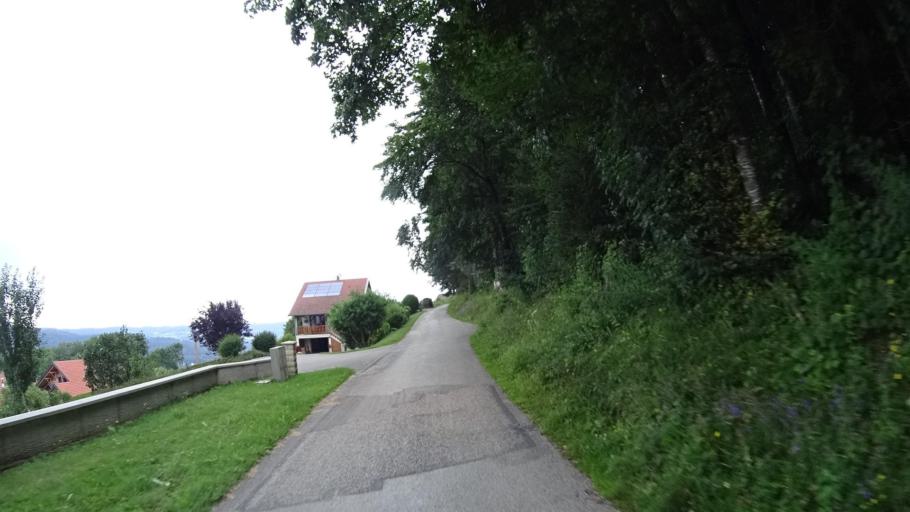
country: FR
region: Franche-Comte
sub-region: Departement du Doubs
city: Les Fourgs
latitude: 46.8222
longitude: 6.3365
